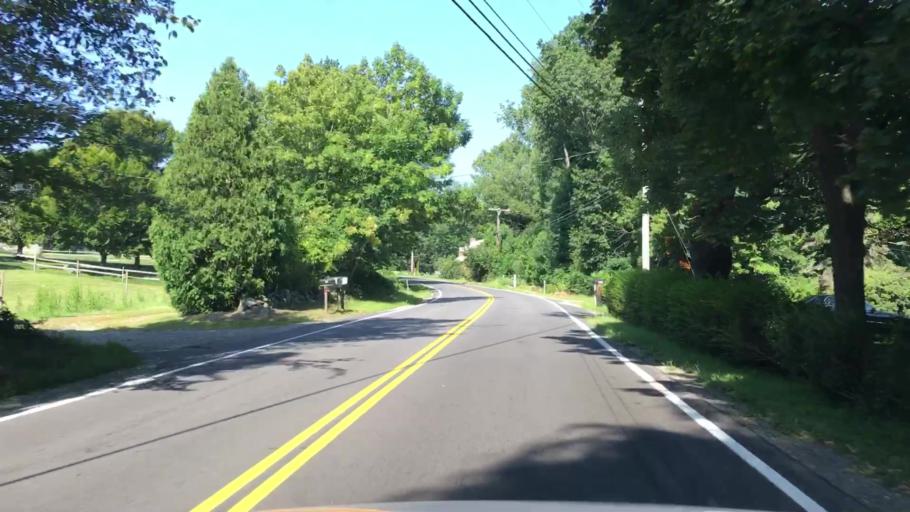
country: US
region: New Hampshire
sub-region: Rockingham County
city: Kensington
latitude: 42.9146
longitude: -70.9683
